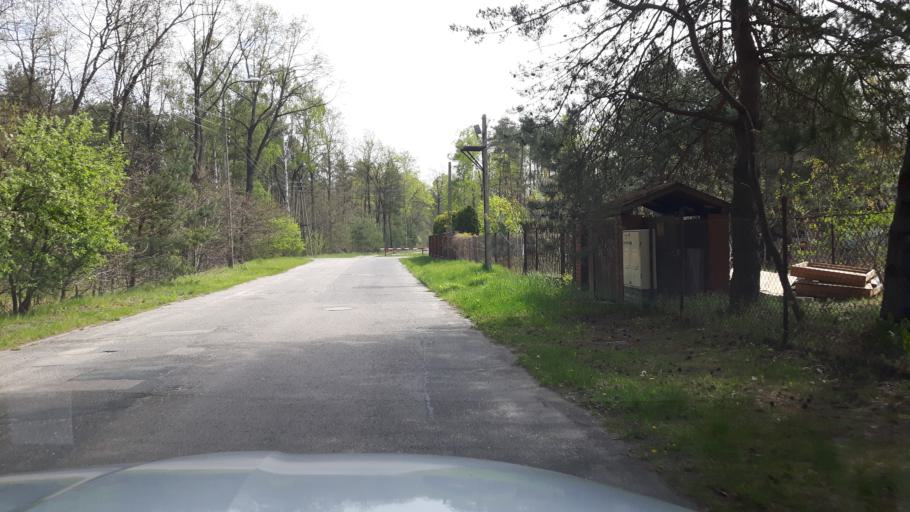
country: PL
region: Masovian Voivodeship
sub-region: Warszawa
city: Wesola
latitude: 52.2527
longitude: 21.2020
